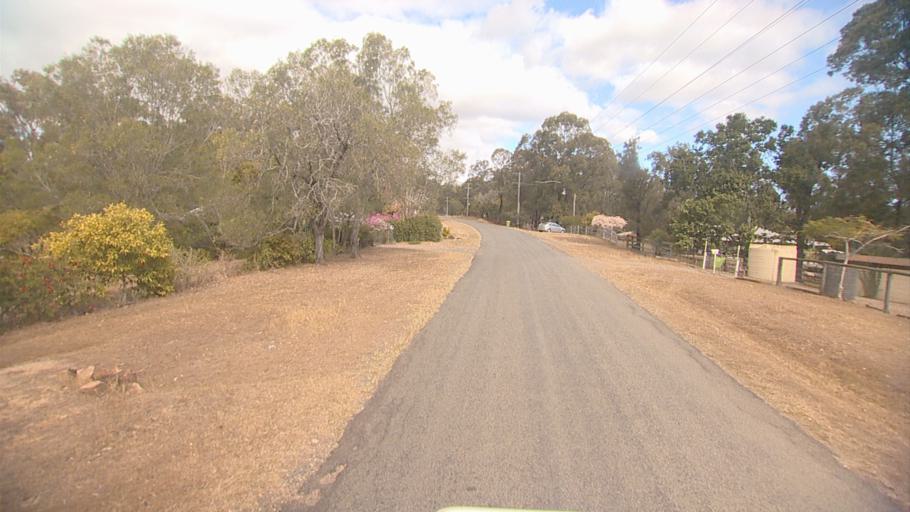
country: AU
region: Queensland
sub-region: Logan
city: Cedar Vale
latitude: -27.8883
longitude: 153.0235
